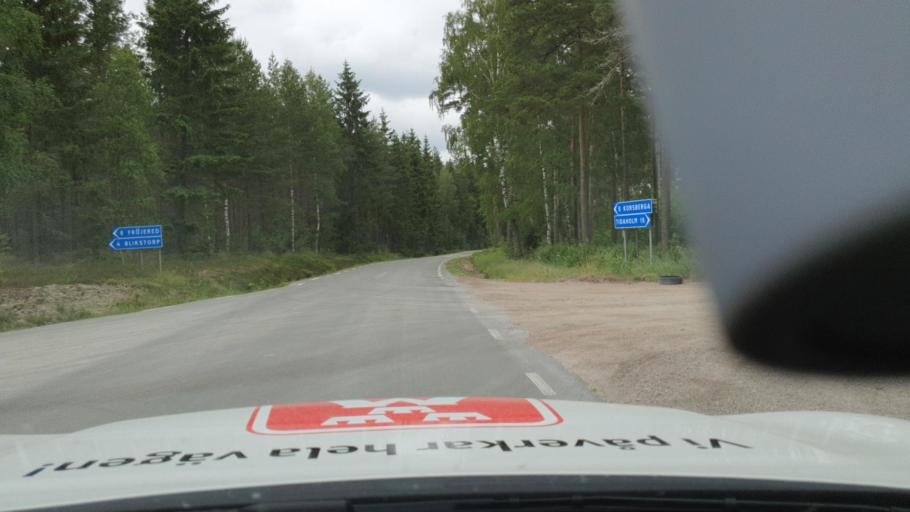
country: SE
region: Vaestra Goetaland
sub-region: Tidaholms Kommun
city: Olofstorp
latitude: 58.2626
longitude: 14.0973
